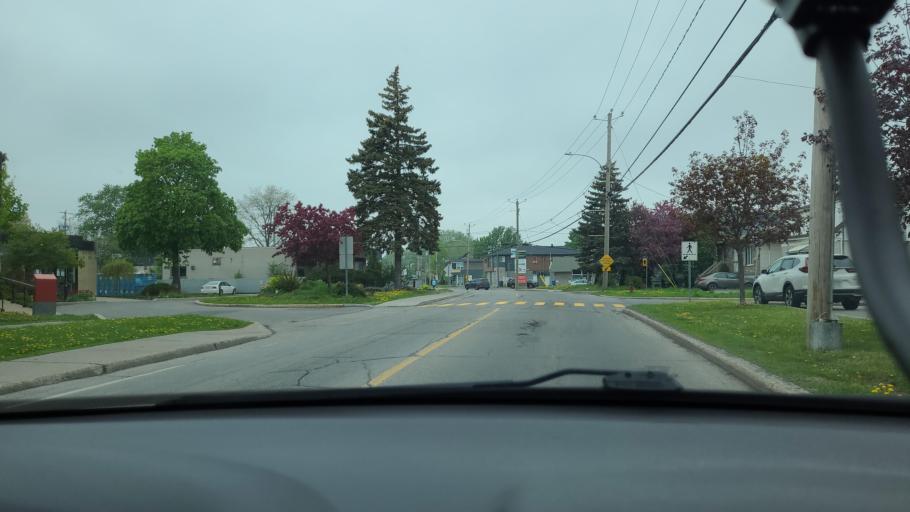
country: CA
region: Quebec
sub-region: Monteregie
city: L'Ile-Perrot
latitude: 45.3936
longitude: -73.9545
